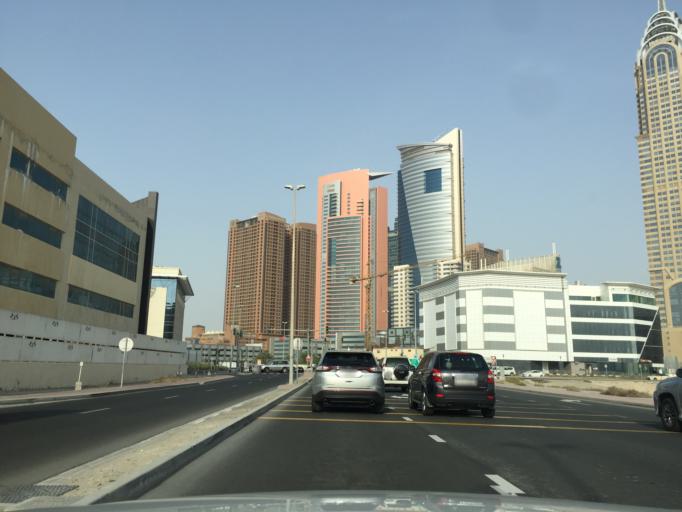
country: AE
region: Dubai
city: Dubai
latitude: 25.1026
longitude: 55.1661
